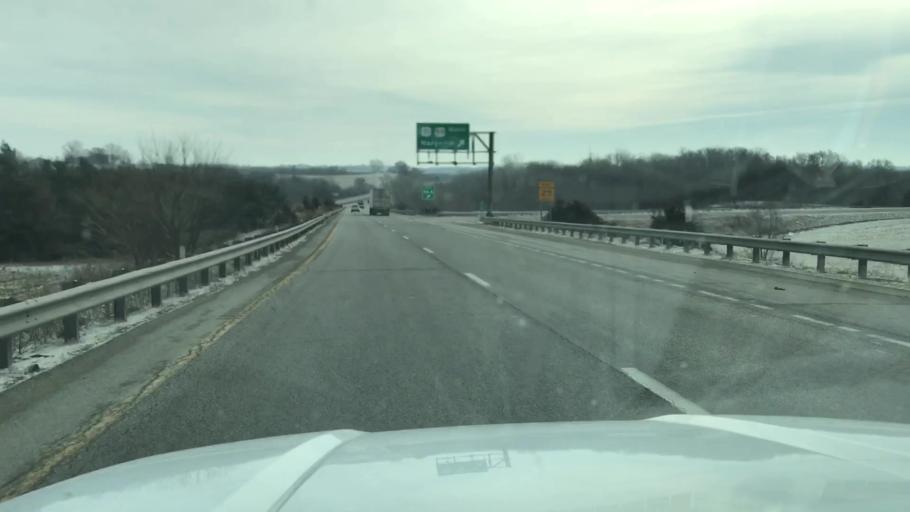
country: US
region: Missouri
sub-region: Andrew County
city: Country Club Village
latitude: 39.8837
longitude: -94.8548
